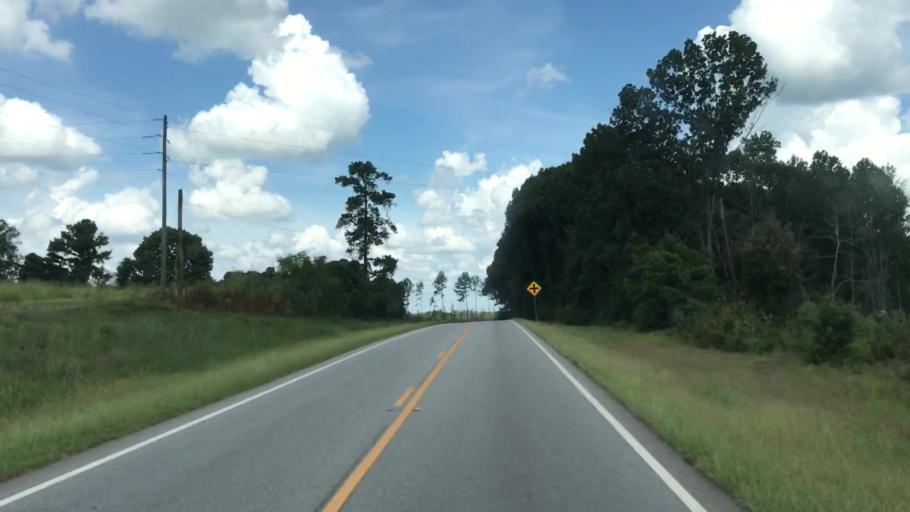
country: US
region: Georgia
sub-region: Greene County
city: Greensboro
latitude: 33.6024
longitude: -83.1977
